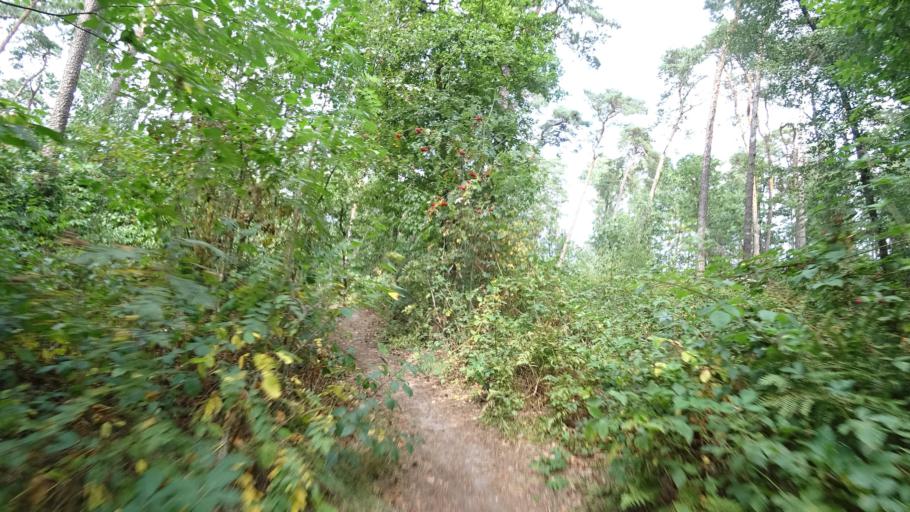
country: DE
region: North Rhine-Westphalia
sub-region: Regierungsbezirk Detmold
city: Steinhagen
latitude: 51.9394
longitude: 8.4553
